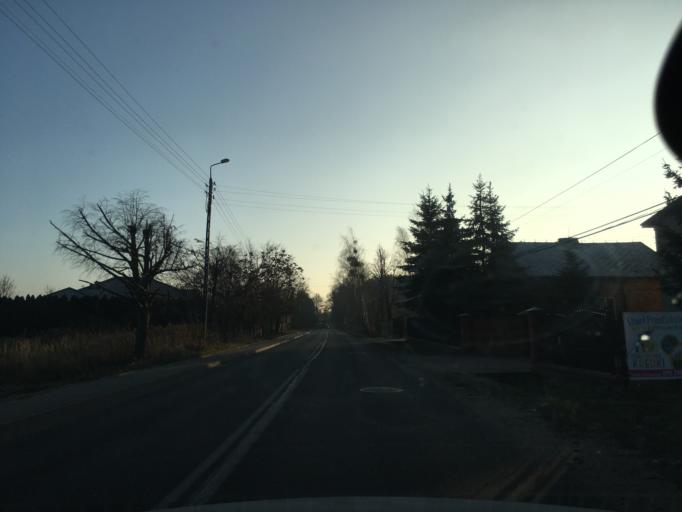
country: PL
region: Masovian Voivodeship
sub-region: Powiat piaseczynski
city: Lesznowola
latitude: 52.0716
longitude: 20.9775
